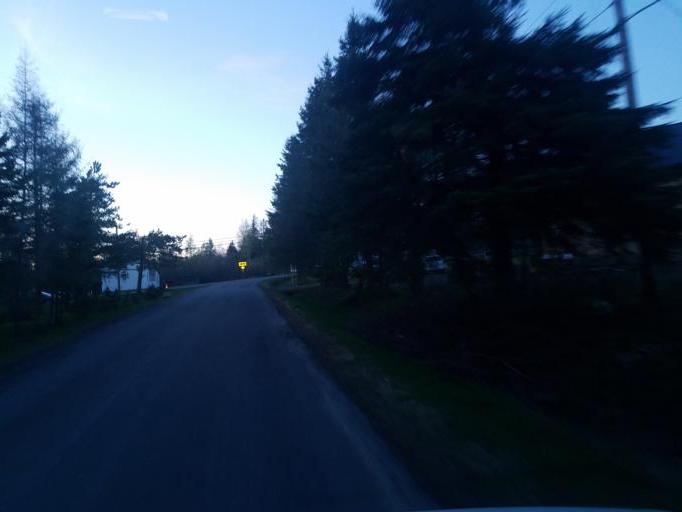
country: US
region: Maine
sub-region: Aroostook County
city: Caribou
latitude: 46.8718
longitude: -68.0713
